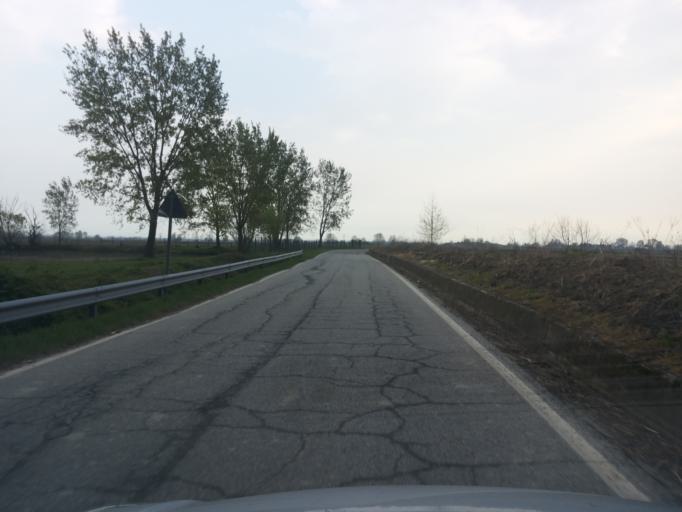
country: IT
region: Piedmont
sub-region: Provincia di Vercelli
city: Caresana
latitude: 45.2031
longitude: 8.4973
